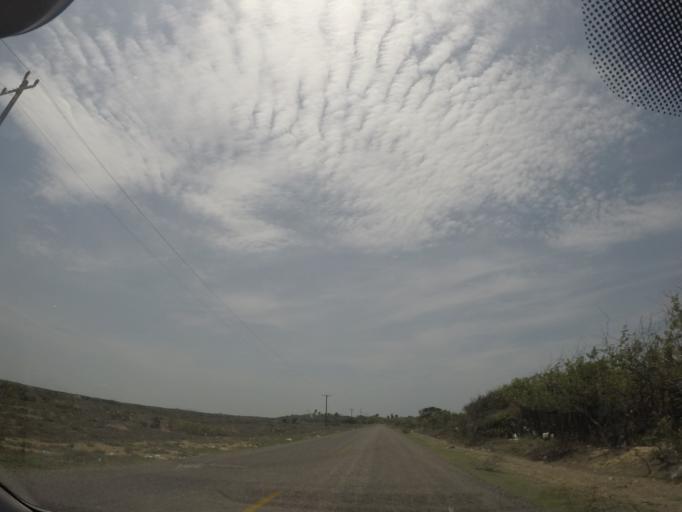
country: MX
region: Oaxaca
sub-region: San Mateo del Mar
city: Colonia Juarez
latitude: 16.2125
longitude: -95.0508
